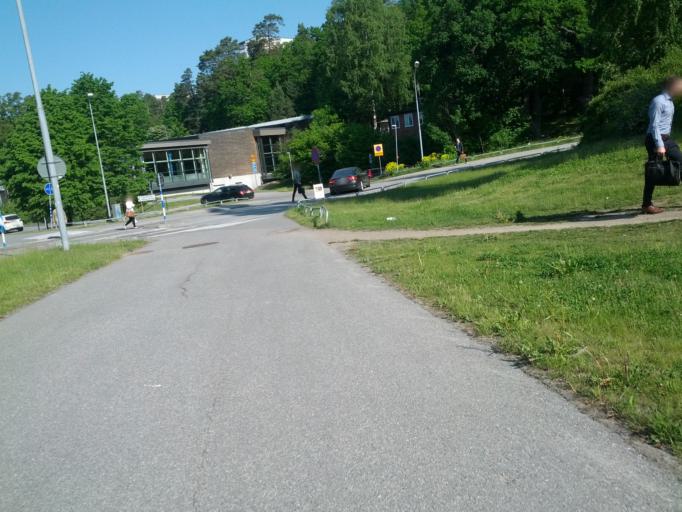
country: SE
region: Stockholm
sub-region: Danderyds Kommun
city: Djursholm
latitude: 59.3936
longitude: 18.0483
